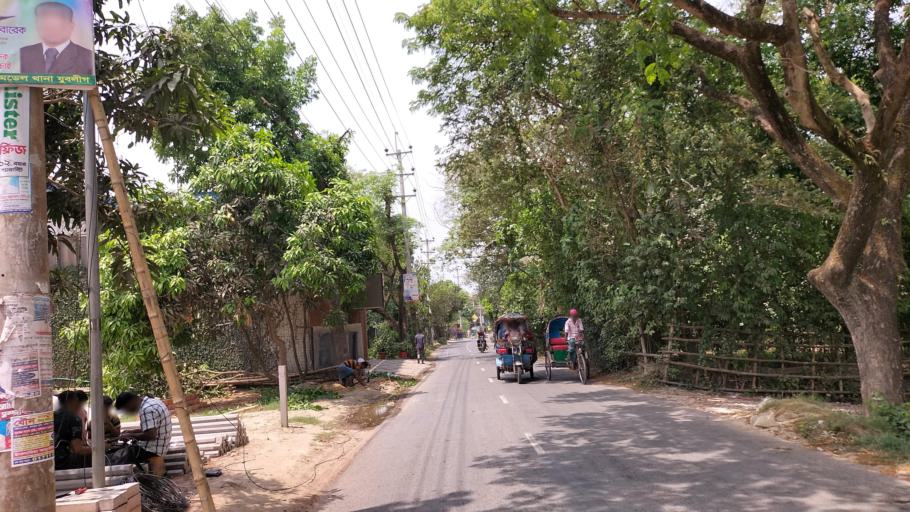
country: BD
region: Dhaka
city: Azimpur
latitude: 23.7290
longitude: 90.2907
